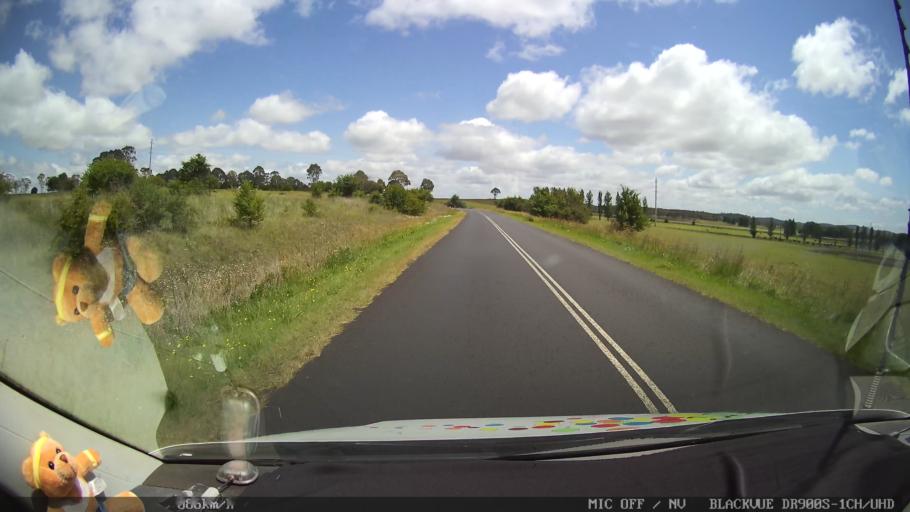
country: AU
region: New South Wales
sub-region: Glen Innes Severn
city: Glen Innes
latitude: -29.7016
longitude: 151.7189
